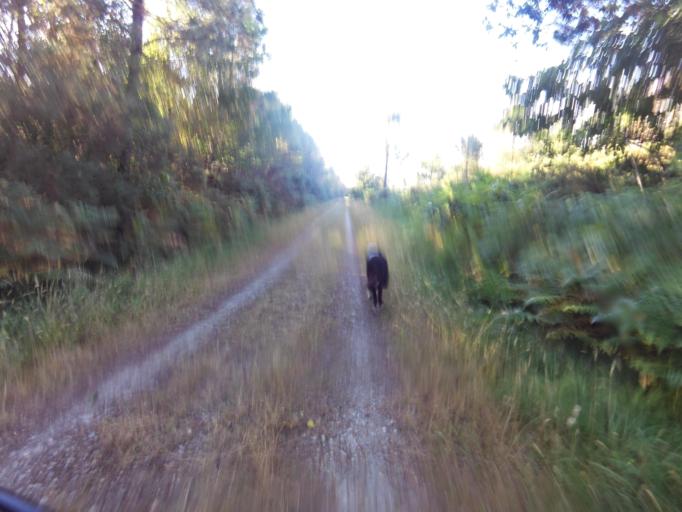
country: FR
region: Brittany
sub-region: Departement du Morbihan
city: Molac
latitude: 47.7535
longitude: -2.4307
